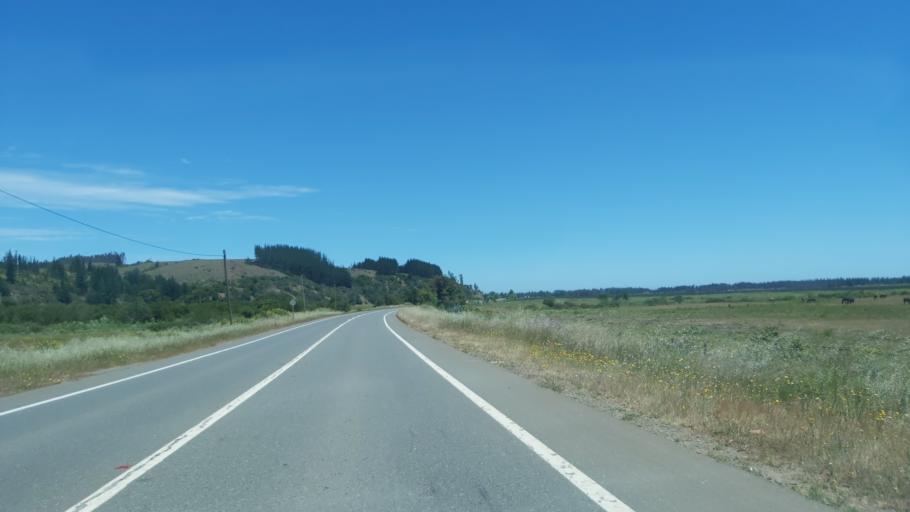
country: CL
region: Maule
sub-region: Provincia de Talca
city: Constitucion
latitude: -35.1547
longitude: -72.2280
